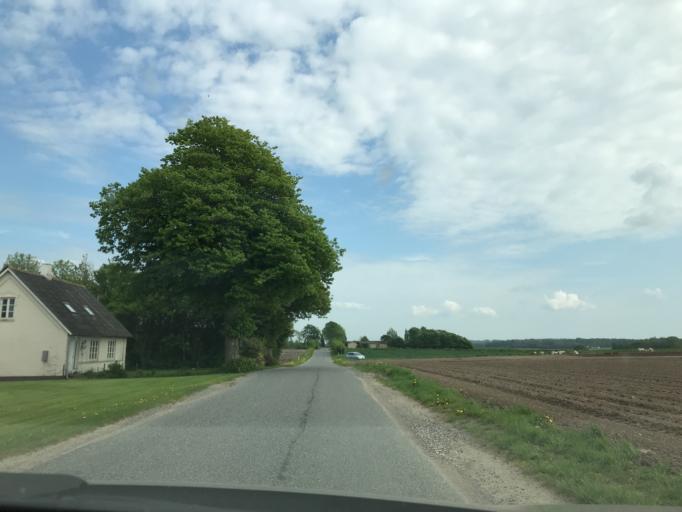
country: DK
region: South Denmark
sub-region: Assens Kommune
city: Assens
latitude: 55.3274
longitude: 9.9042
